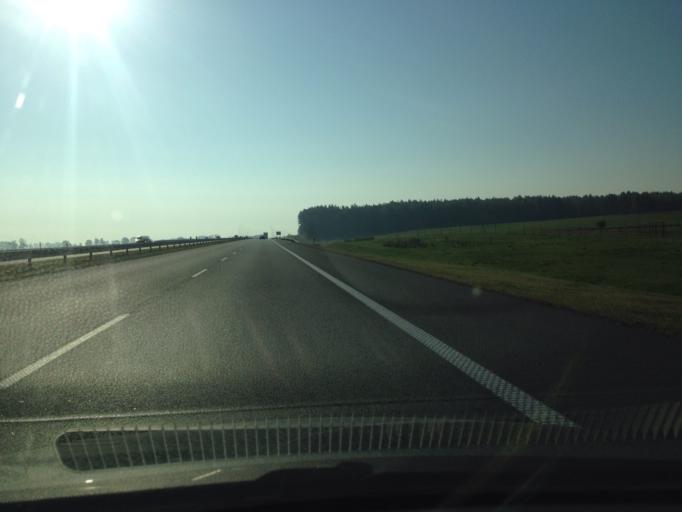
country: PL
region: Pomeranian Voivodeship
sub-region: Powiat gdanski
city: Legowo
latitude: 54.2018
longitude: 18.6218
